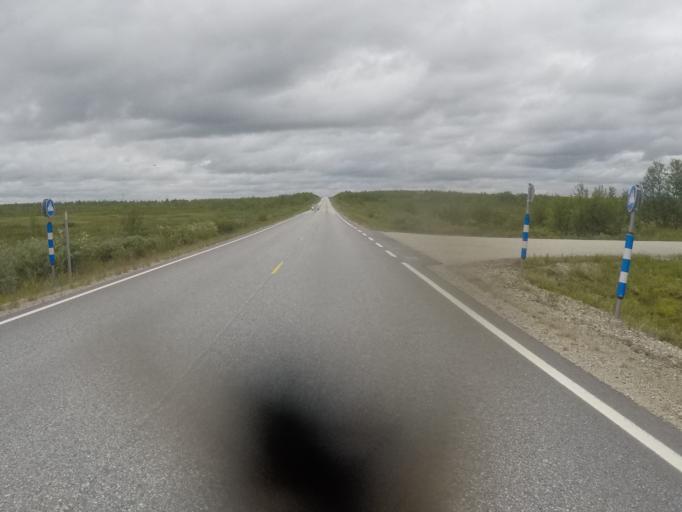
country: NO
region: Finnmark Fylke
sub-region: Kautokeino
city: Kautokeino
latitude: 68.7908
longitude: 23.2971
